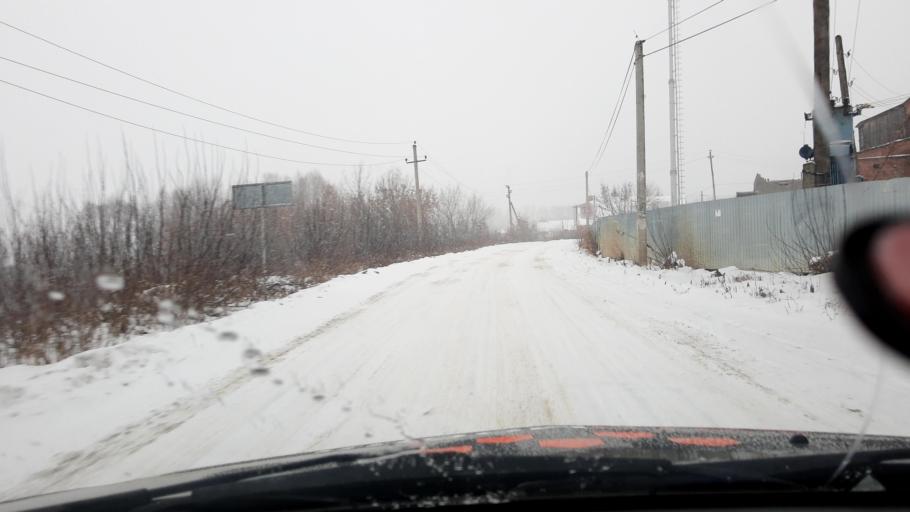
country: RU
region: Bashkortostan
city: Ufa
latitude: 54.5442
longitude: 55.9414
